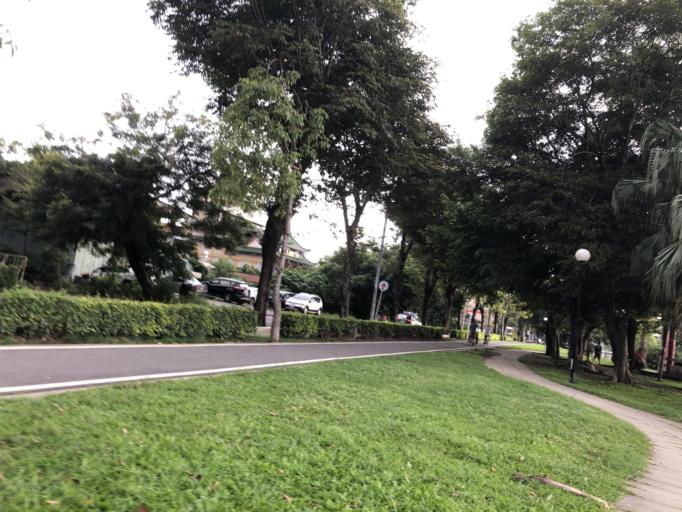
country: TW
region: Kaohsiung
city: Kaohsiung
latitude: 22.6853
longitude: 120.2996
